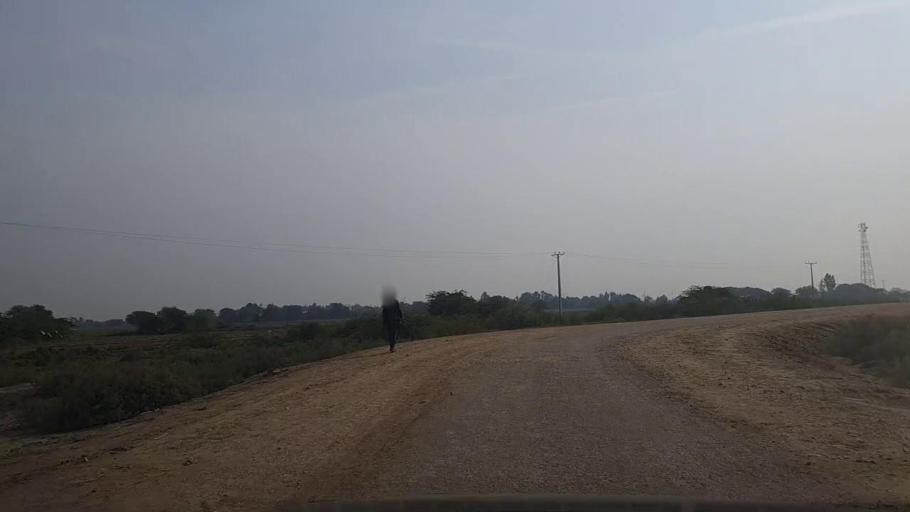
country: PK
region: Sindh
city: Mirpur Sakro
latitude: 24.4091
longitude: 67.7442
